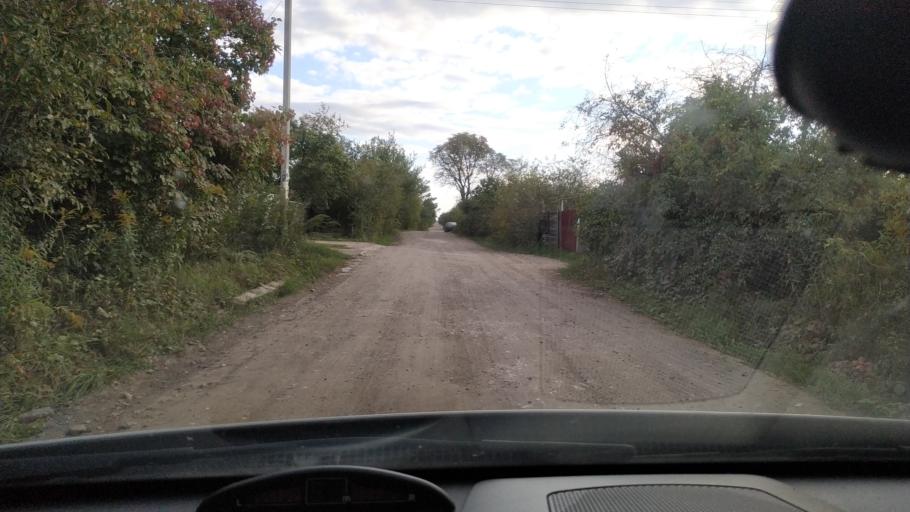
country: RU
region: Rjazan
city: Polyany
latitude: 54.5593
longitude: 39.8781
